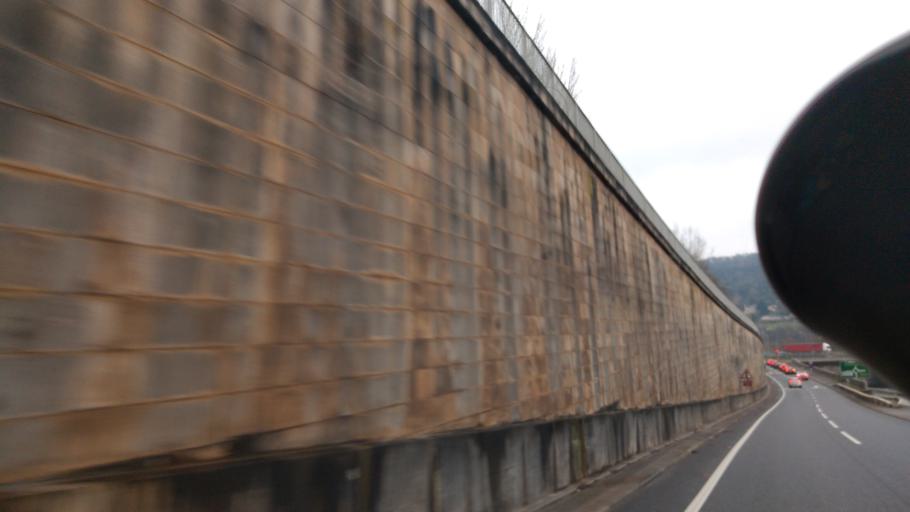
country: GB
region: England
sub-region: Bath and North East Somerset
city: Bath
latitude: 51.4008
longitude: -2.3379
